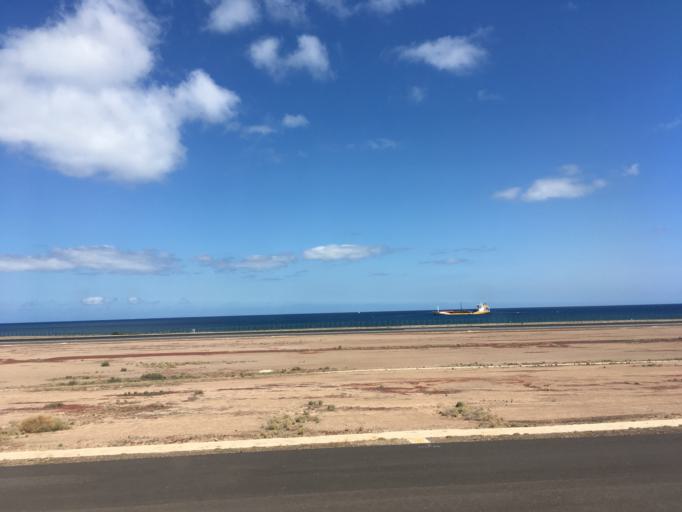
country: ES
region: Canary Islands
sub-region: Provincia de Las Palmas
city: Tias
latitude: 28.9426
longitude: -13.6089
